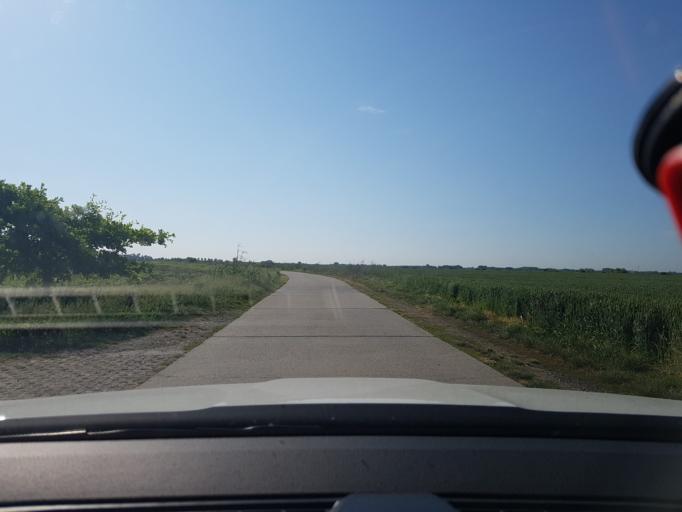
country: HU
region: Tolna
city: Decs
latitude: 46.2783
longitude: 18.7059
